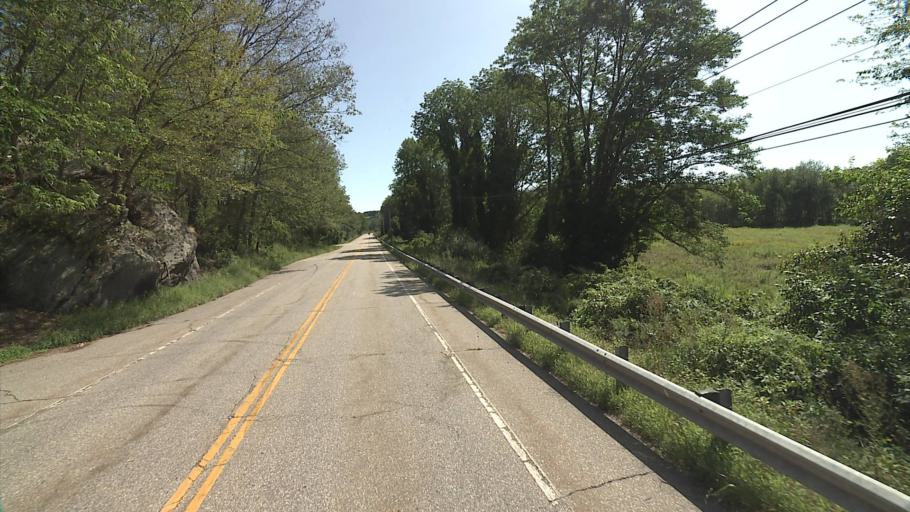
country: US
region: Connecticut
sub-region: New London County
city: Baltic
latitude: 41.6333
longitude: -72.1378
